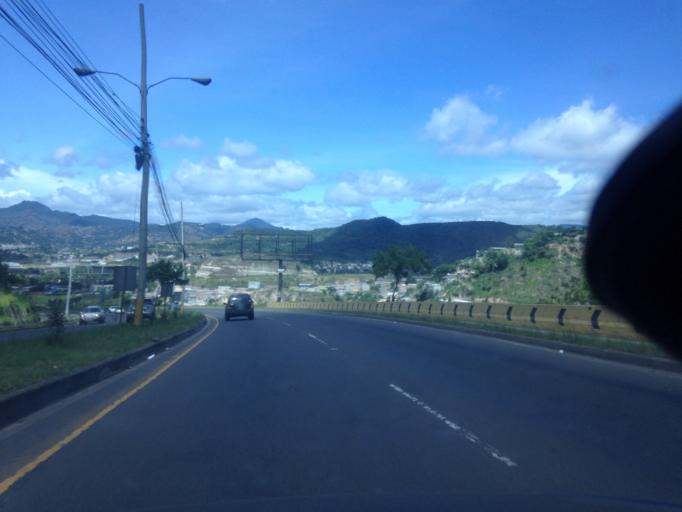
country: HN
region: Francisco Morazan
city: Yaguacire
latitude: 14.0448
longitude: -87.2208
